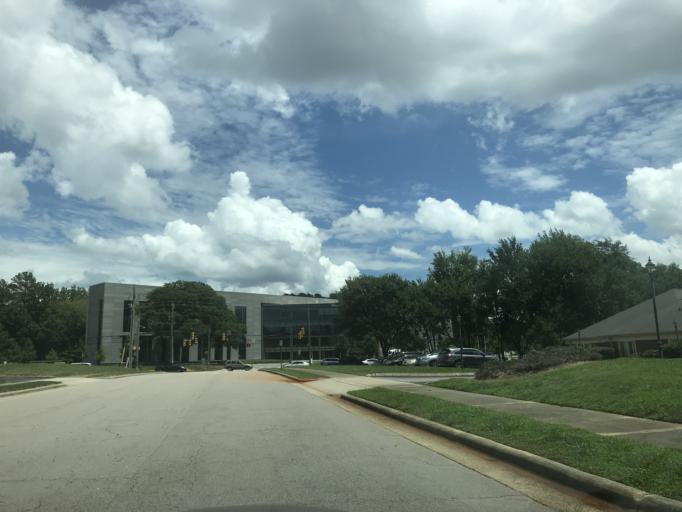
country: US
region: North Carolina
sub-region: Wake County
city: Raleigh
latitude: 35.8330
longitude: -78.6185
